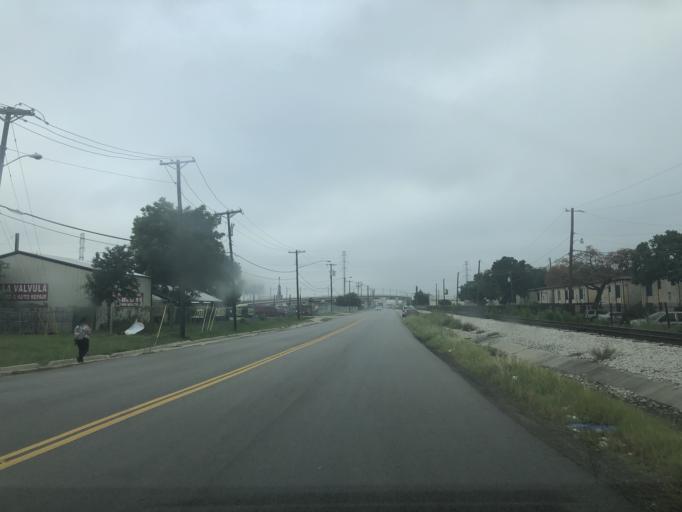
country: US
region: Texas
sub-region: Dallas County
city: Farmers Branch
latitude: 32.8560
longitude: -96.8775
